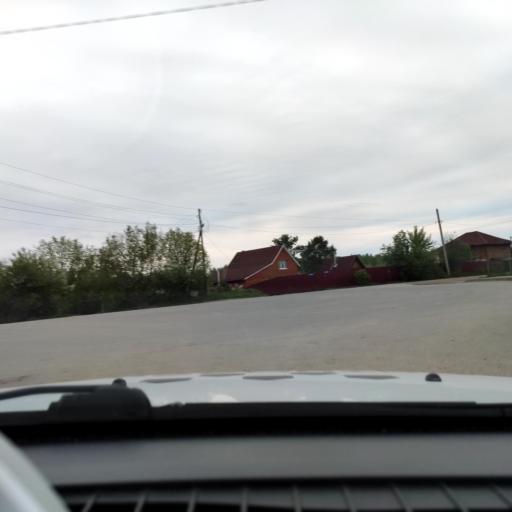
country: RU
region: Perm
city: Kondratovo
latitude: 58.0142
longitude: 56.0419
